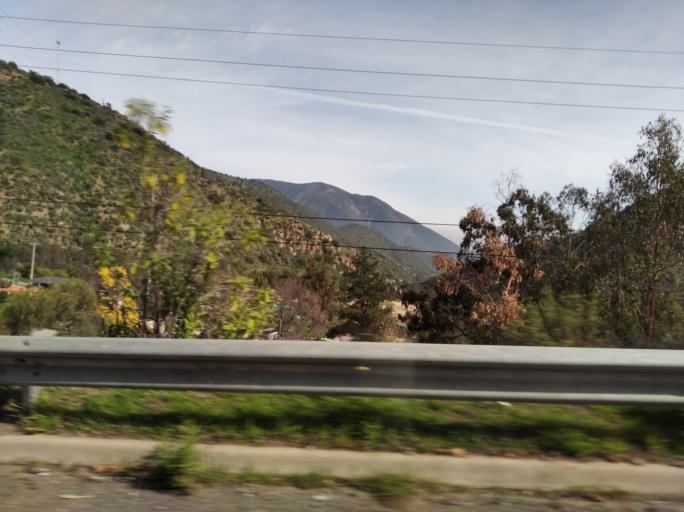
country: CL
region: Valparaiso
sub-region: Provincia de Marga Marga
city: Limache
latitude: -33.0642
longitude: -71.0648
